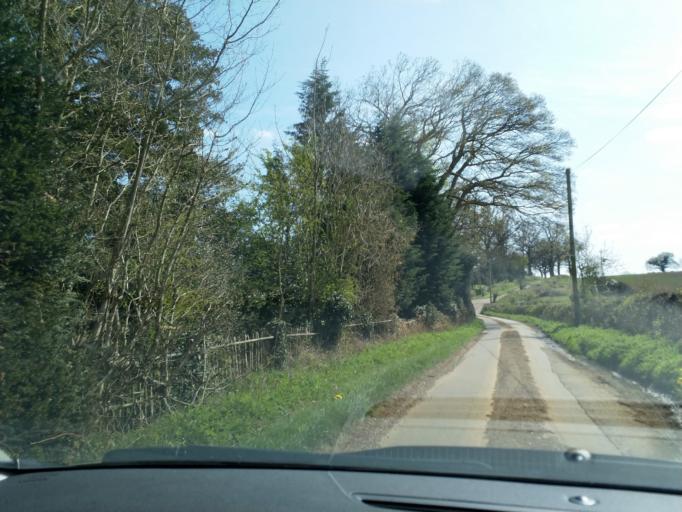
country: GB
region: England
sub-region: Oxfordshire
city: Adderbury
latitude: 52.0690
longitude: -1.2459
